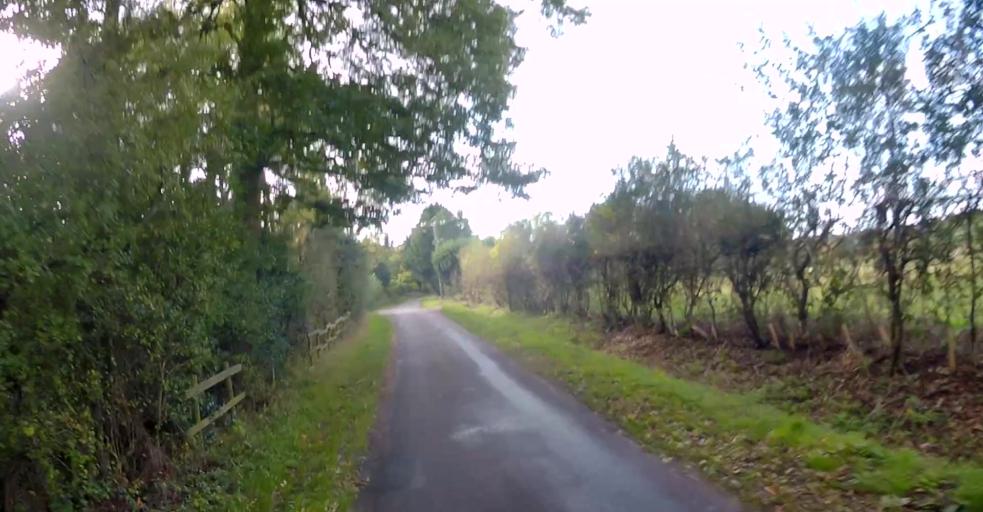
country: GB
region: England
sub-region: Surrey
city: Farnham
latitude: 51.2076
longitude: -0.8395
